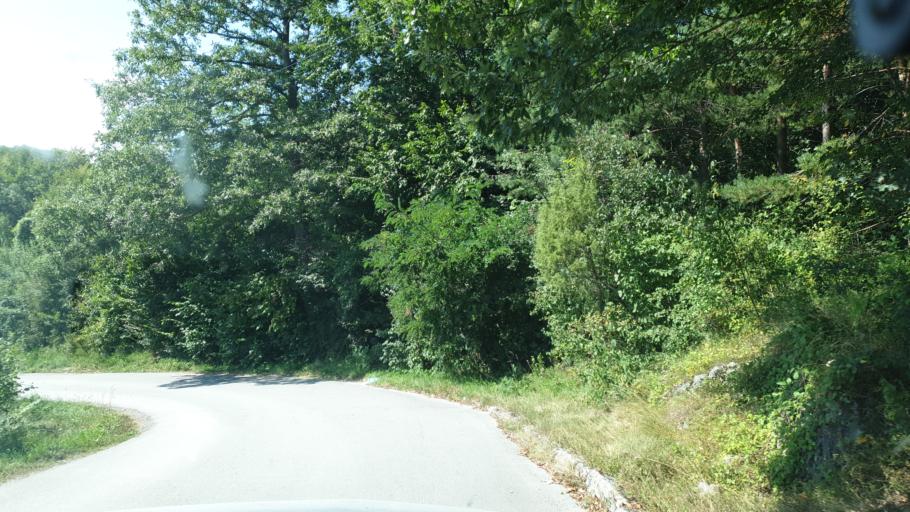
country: RS
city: Zlatibor
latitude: 43.6554
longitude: 19.8306
